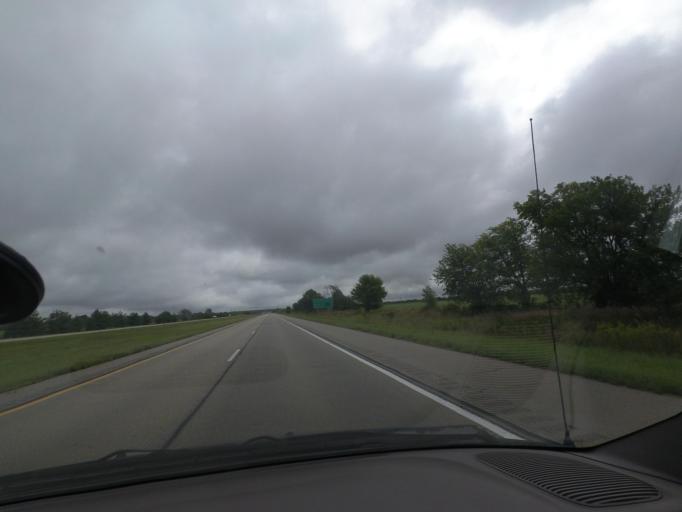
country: US
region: Illinois
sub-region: Piatt County
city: Monticello
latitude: 40.0306
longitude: -88.6384
